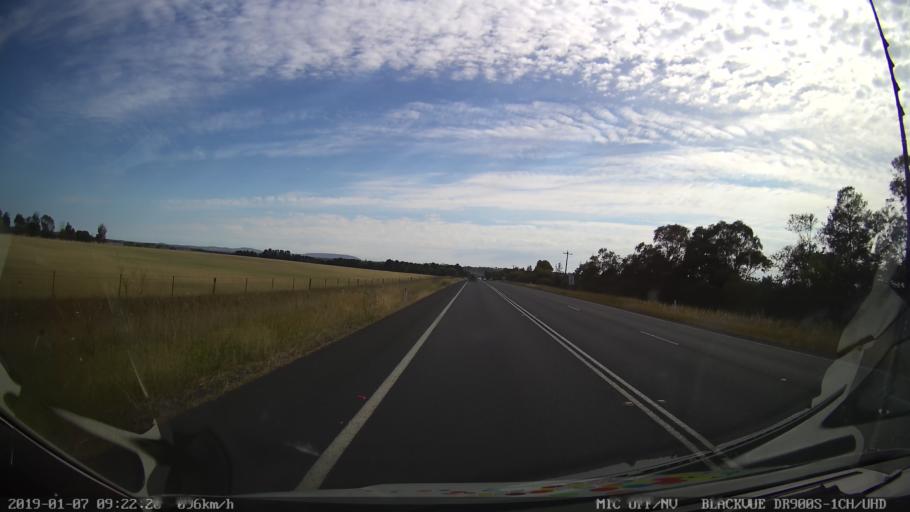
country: AU
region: New South Wales
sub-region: Armidale Dumaresq
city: Armidale
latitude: -30.5696
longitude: 151.5746
